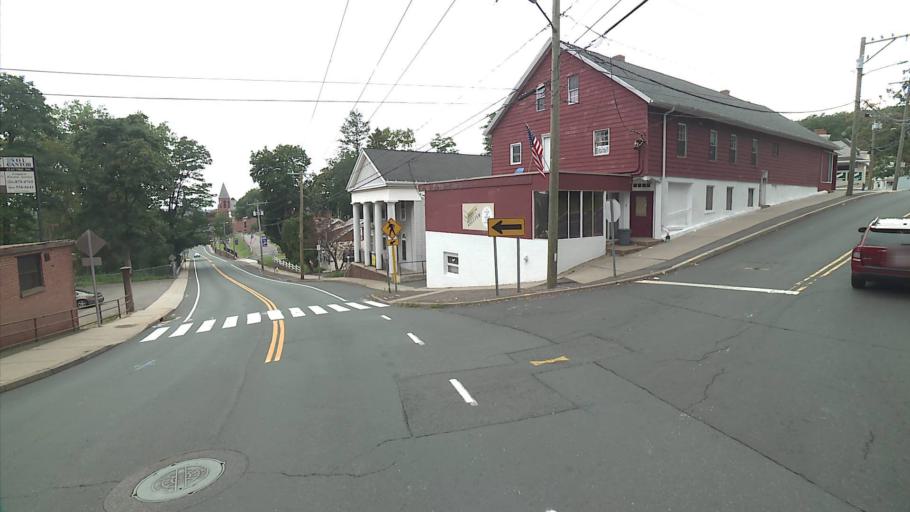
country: US
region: Connecticut
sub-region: Tolland County
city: Rockville
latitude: 41.8681
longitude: -72.4434
